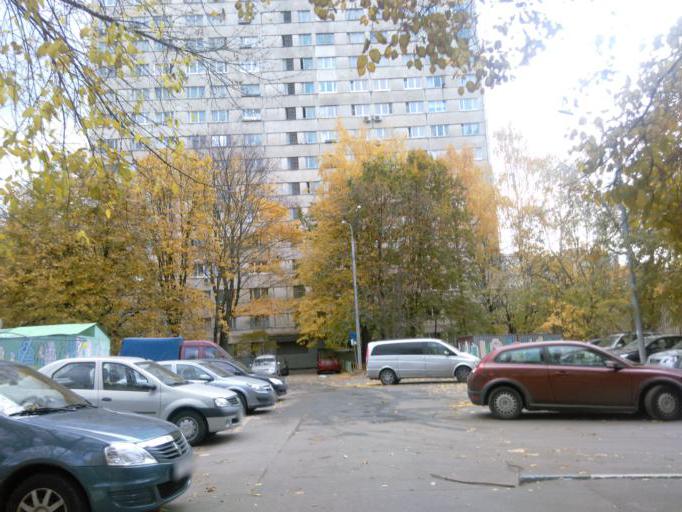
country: RU
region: Moscow
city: Troparevo
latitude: 55.6585
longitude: 37.5137
